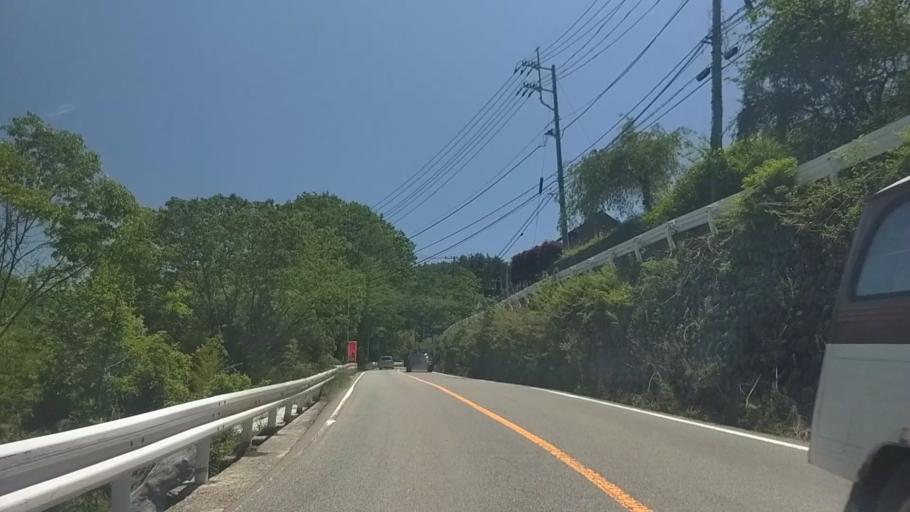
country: JP
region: Yamanashi
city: Nirasaki
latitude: 35.8757
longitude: 138.4284
